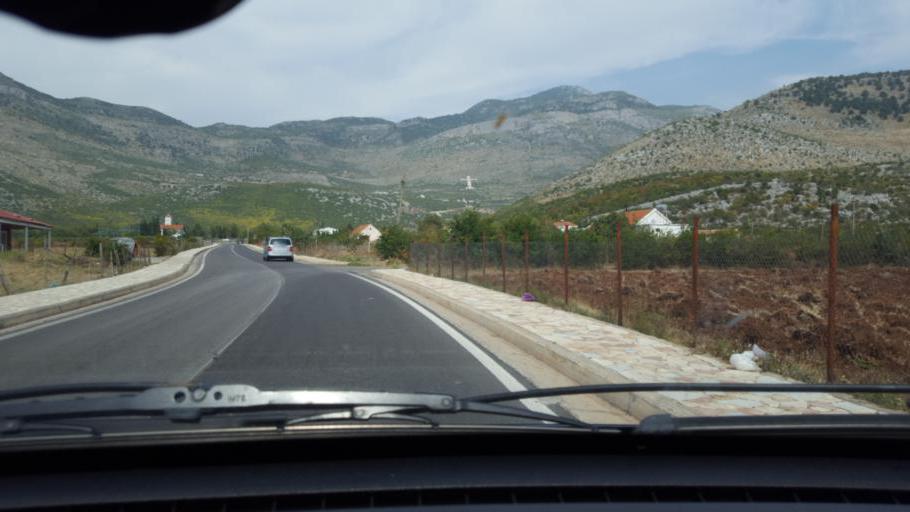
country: AL
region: Shkoder
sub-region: Rrethi i Malesia e Madhe
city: Hot
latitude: 42.3551
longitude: 19.4430
